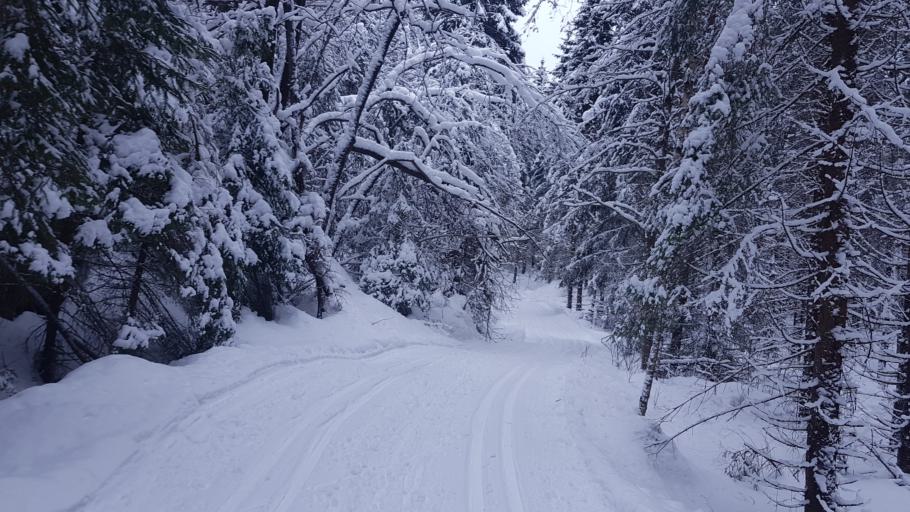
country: NO
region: Akershus
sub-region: Lorenskog
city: Kjenn
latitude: 59.9006
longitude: 10.8769
